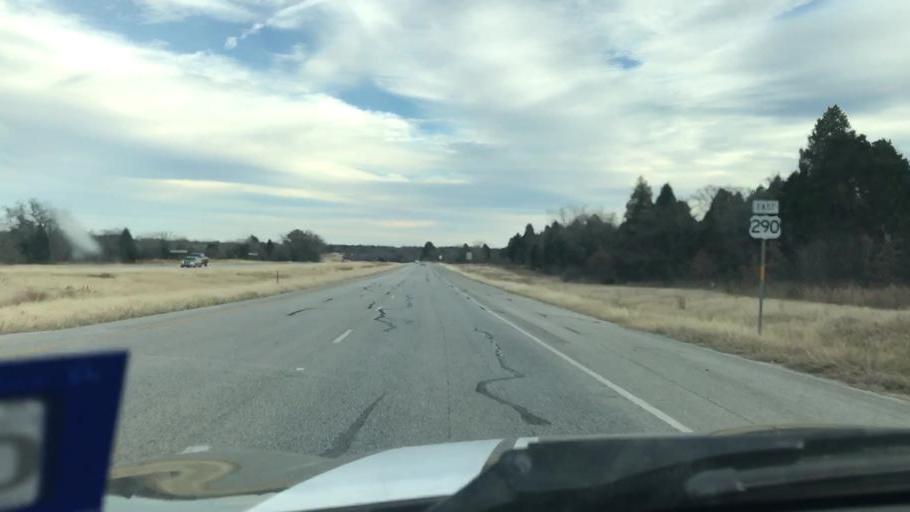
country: US
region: Texas
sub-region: Bastrop County
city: Elgin
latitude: 30.3102
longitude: -97.3051
